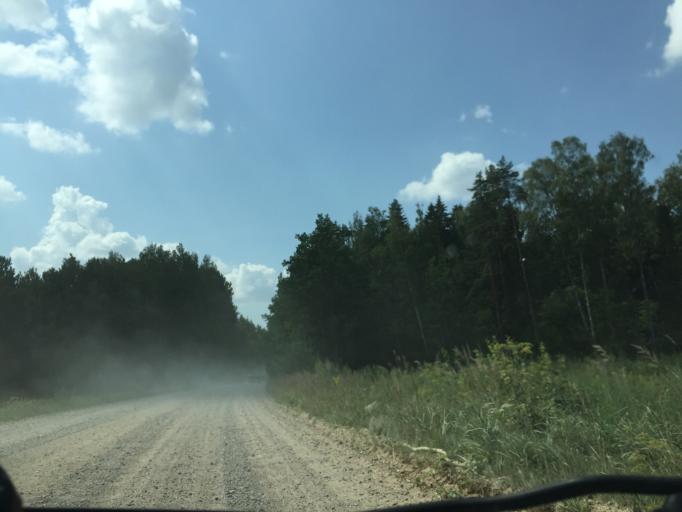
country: LV
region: Tervete
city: Zelmeni
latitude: 56.3961
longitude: 23.3202
